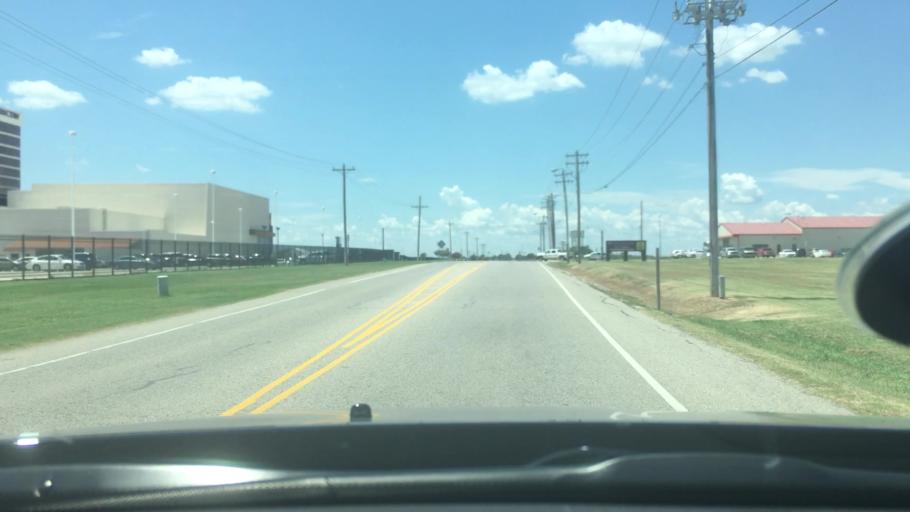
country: US
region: Oklahoma
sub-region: Bryan County
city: Calera
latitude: 33.9542
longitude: -96.4107
